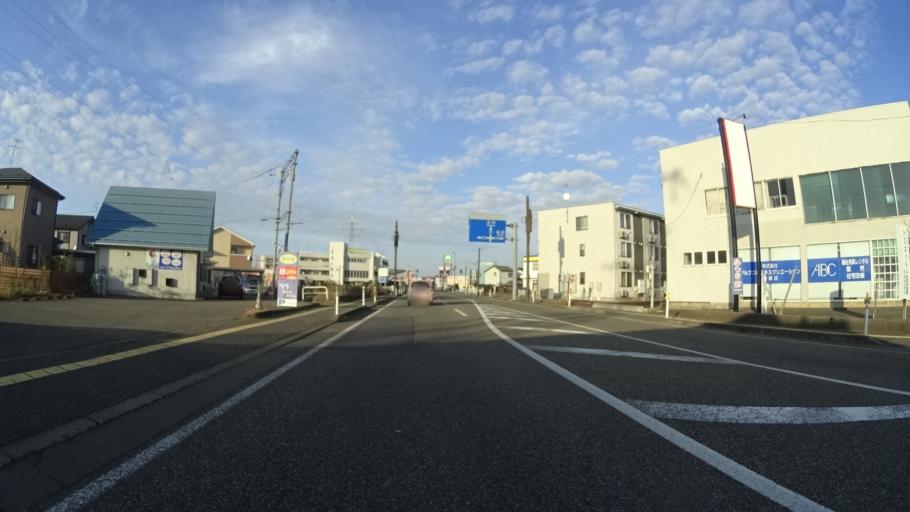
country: JP
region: Niigata
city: Kashiwazaki
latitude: 37.3714
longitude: 138.5781
